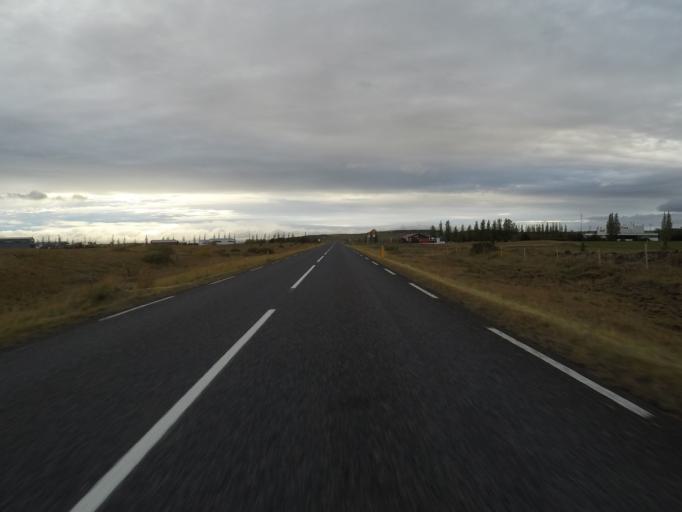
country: IS
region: South
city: Vestmannaeyjar
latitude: 64.0410
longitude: -20.2472
